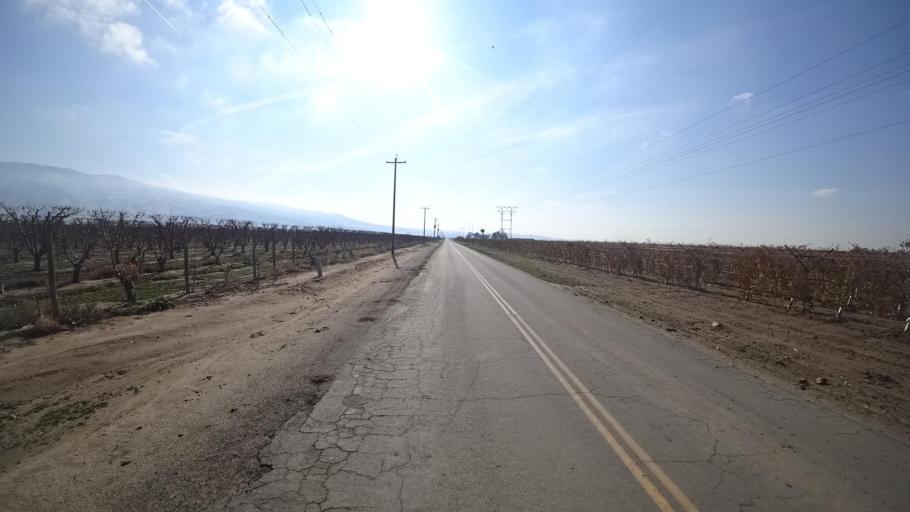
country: US
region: California
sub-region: Kern County
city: Arvin
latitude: 35.2163
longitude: -118.8062
